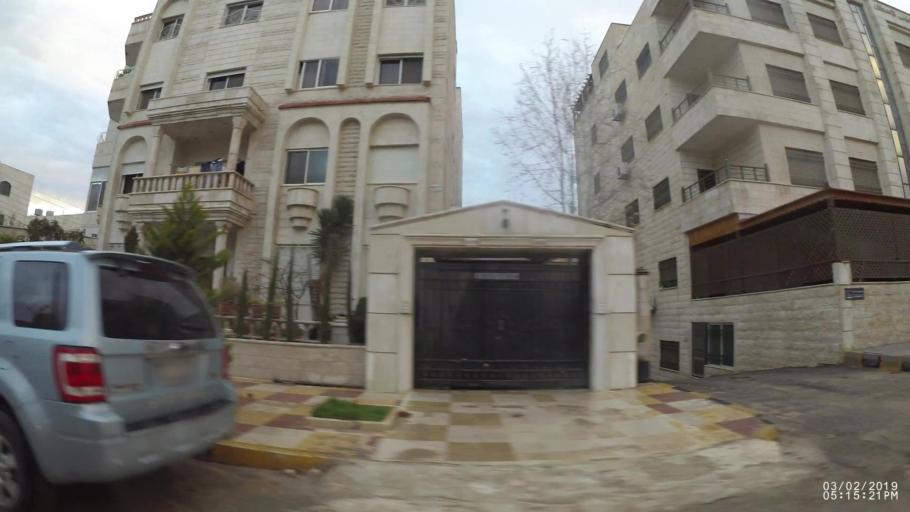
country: JO
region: Amman
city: Amman
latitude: 31.9876
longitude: 35.9118
